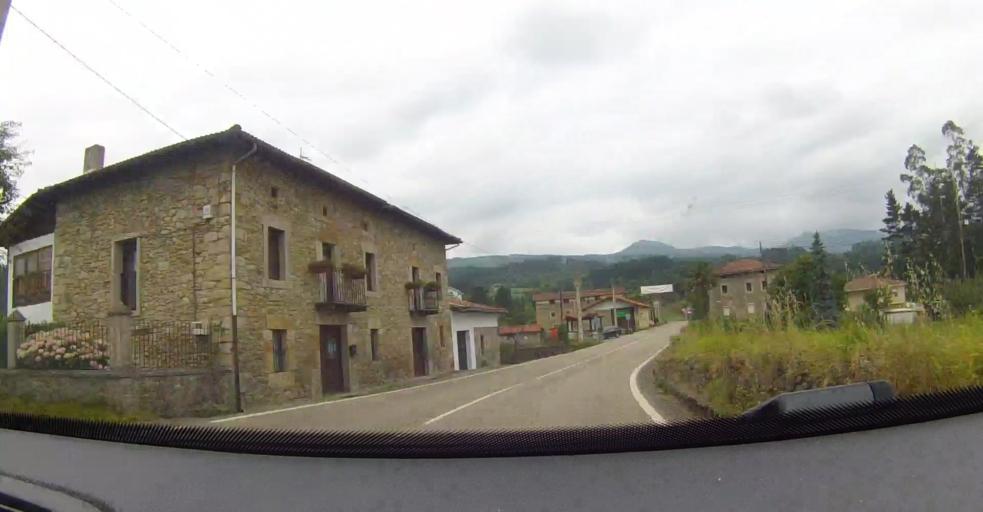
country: ES
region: Basque Country
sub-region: Bizkaia
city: Balmaseda
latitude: 43.2439
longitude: -3.2636
